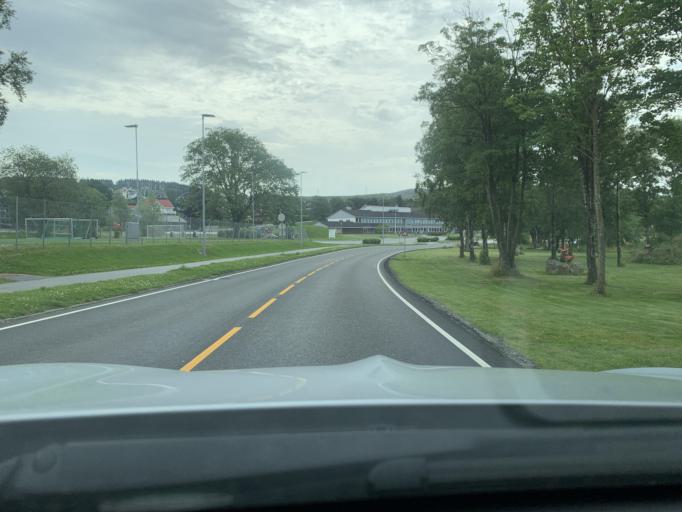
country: NO
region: Rogaland
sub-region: Sandnes
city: Sandnes
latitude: 58.7739
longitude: 5.7250
